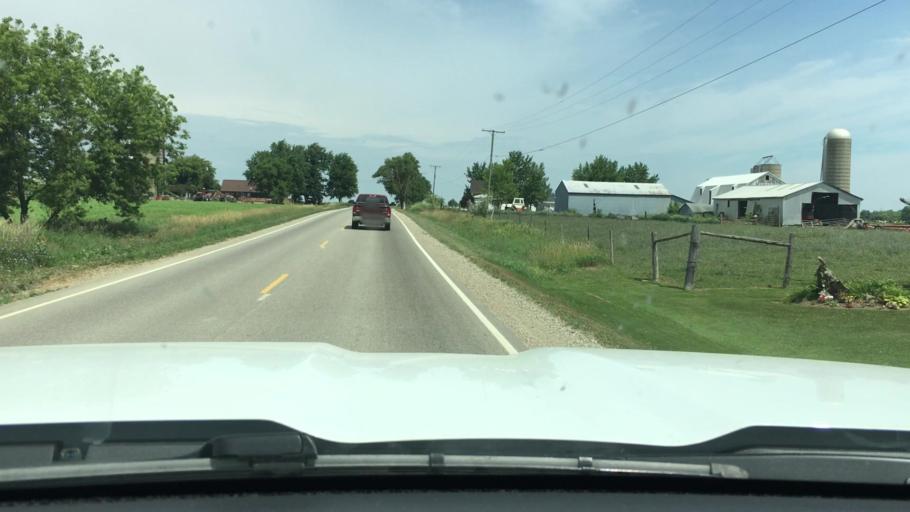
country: US
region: Michigan
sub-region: Sanilac County
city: Brown City
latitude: 43.2744
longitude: -82.9824
